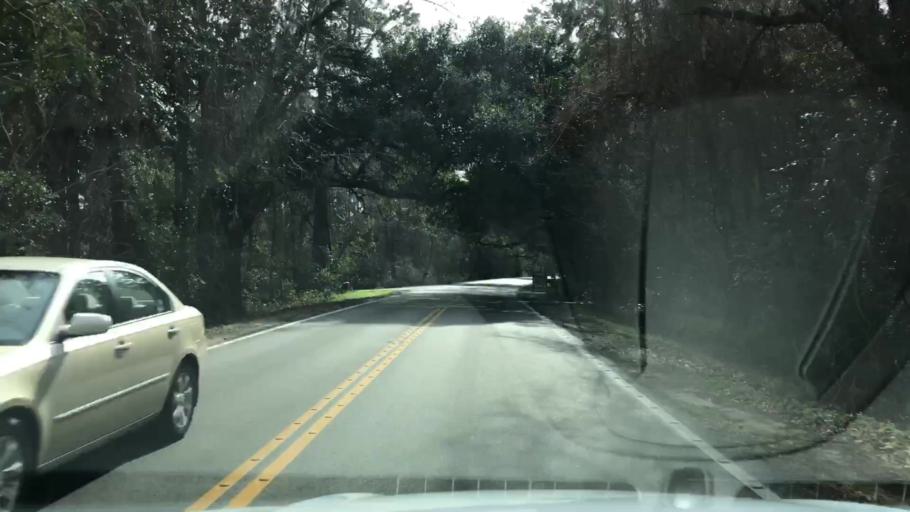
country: US
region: South Carolina
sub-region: Charleston County
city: Shell Point
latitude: 32.7268
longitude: -80.0245
